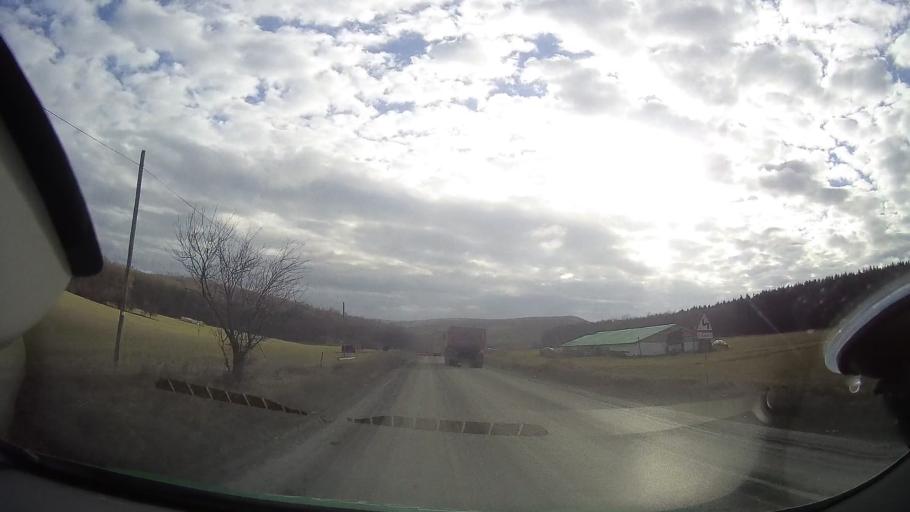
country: RO
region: Cluj
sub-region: Comuna Savadisla
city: Savadisla
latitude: 46.6491
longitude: 23.4610
